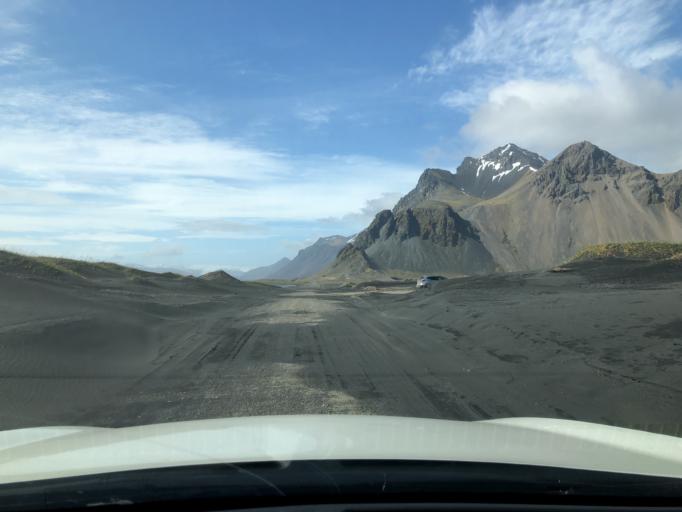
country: IS
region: East
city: Hoefn
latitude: 64.2445
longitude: -14.9721
